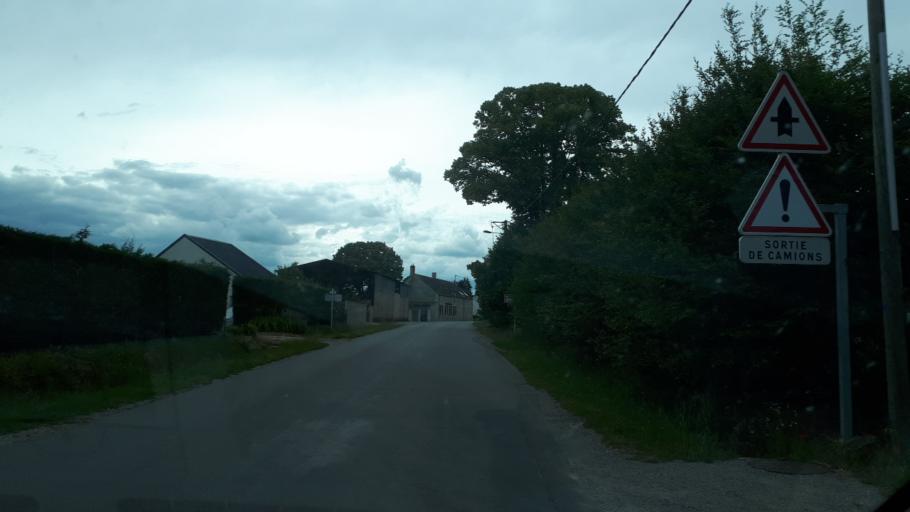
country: FR
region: Centre
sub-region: Departement de l'Indre
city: Reuilly
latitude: 47.0890
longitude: 2.0320
